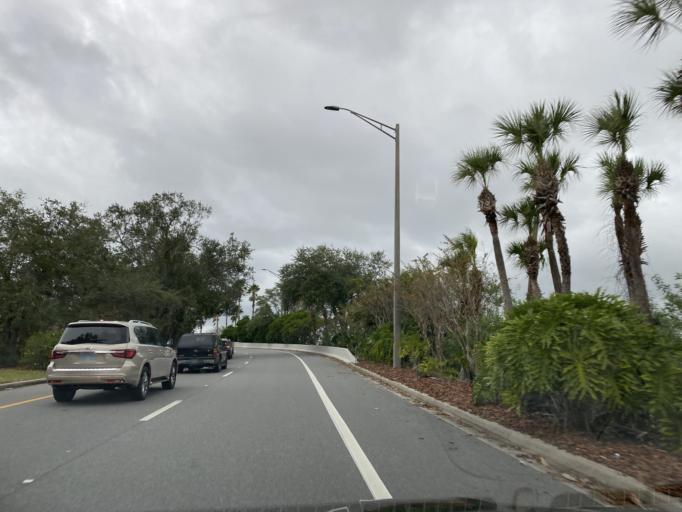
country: US
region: Florida
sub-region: Orange County
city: Belle Isle
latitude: 28.4374
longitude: -81.3072
